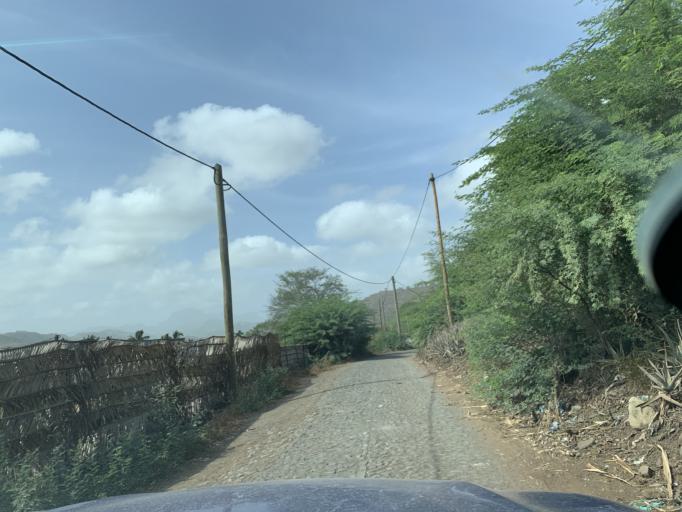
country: CV
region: Santa Cruz
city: Pedra Badejo
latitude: 15.1317
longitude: -23.5335
